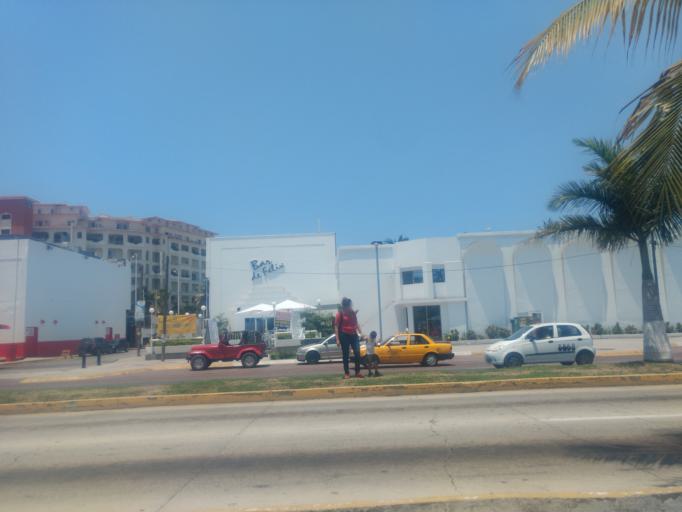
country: MX
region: Colima
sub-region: Manzanillo
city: Manzanillo
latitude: 19.1015
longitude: -104.3262
